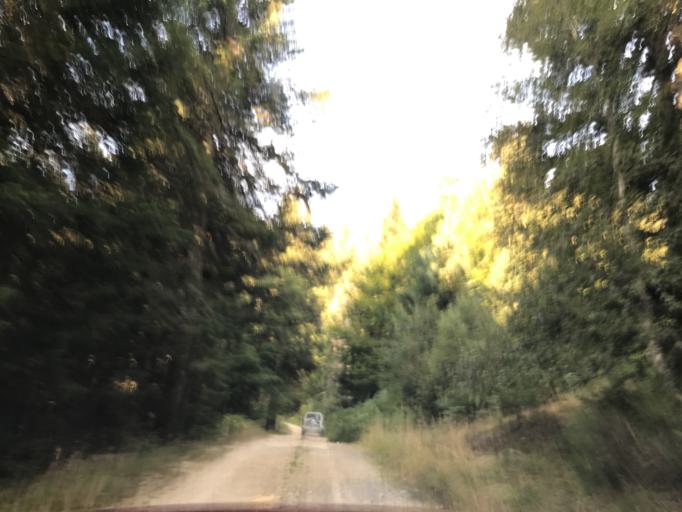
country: FR
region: Rhone-Alpes
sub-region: Departement de la Loire
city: Noiretable
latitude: 45.7619
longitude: 3.7614
